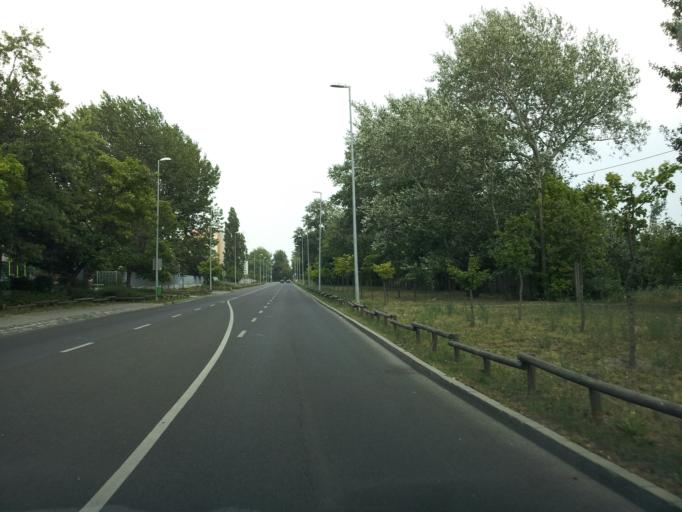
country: HU
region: Budapest
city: Budapest XI. keruelet
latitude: 47.4552
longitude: 19.0470
